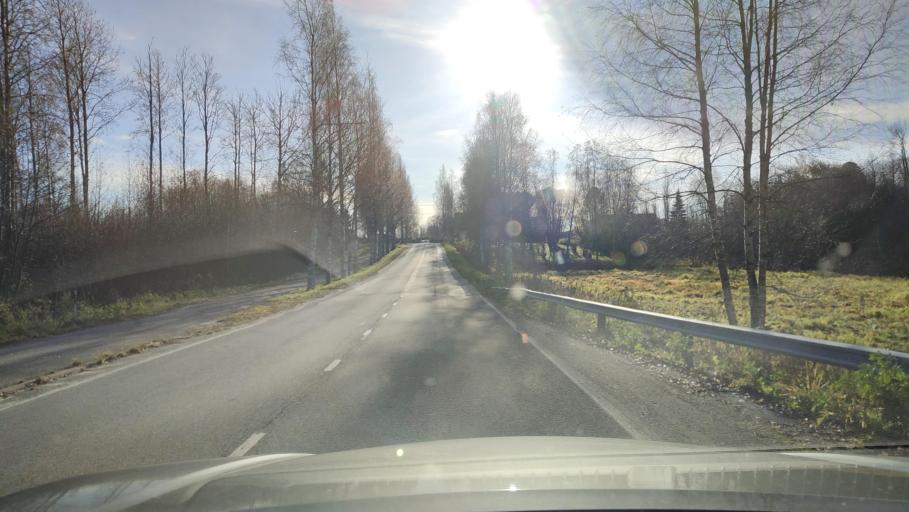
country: FI
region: Southern Ostrobothnia
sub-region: Suupohja
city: Teuva
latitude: 62.4773
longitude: 21.7405
